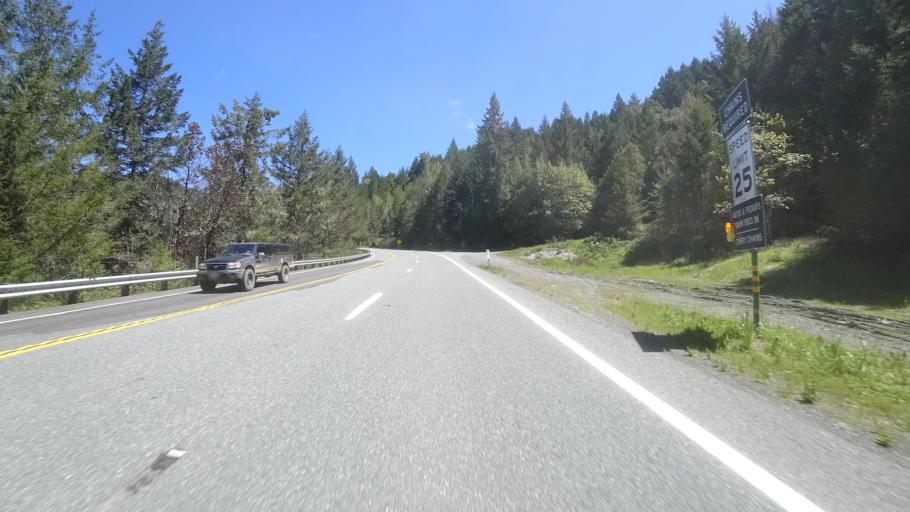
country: US
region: California
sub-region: Humboldt County
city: Willow Creek
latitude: 40.9131
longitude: -123.8072
